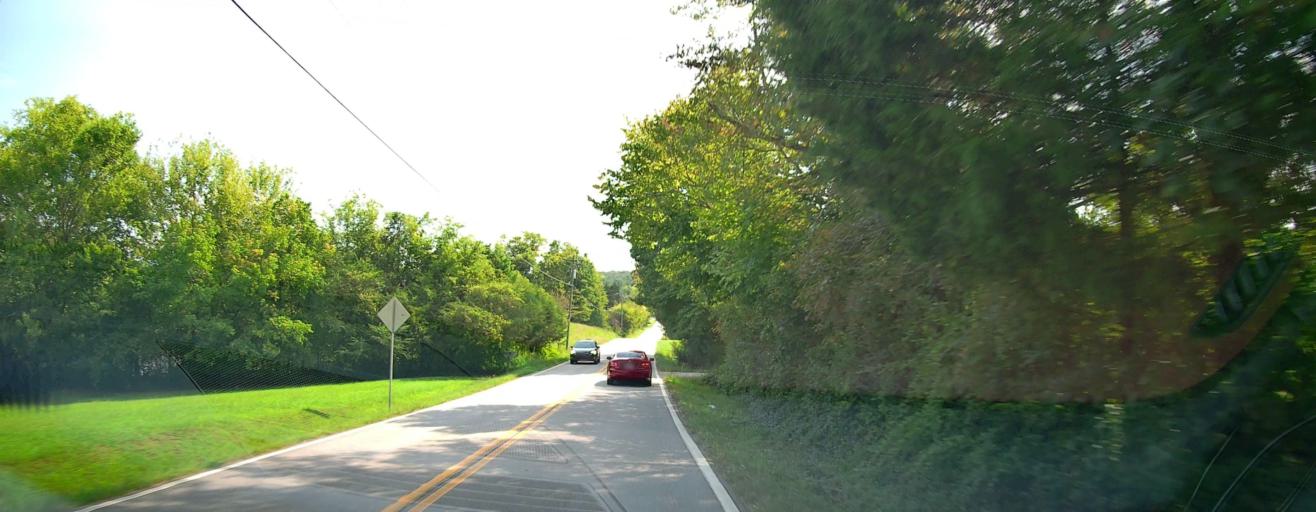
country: US
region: Georgia
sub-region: Catoosa County
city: Ringgold
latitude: 34.9353
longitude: -85.0840
